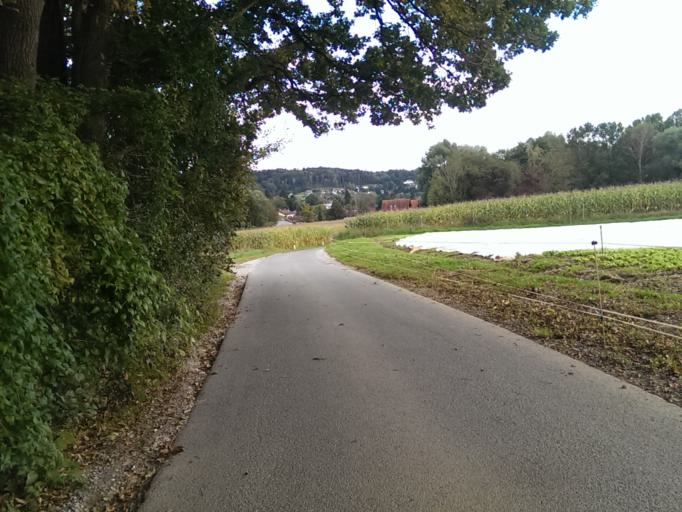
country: AT
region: Styria
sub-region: Politischer Bezirk Graz-Umgebung
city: Raaba
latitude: 47.0417
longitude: 15.4948
